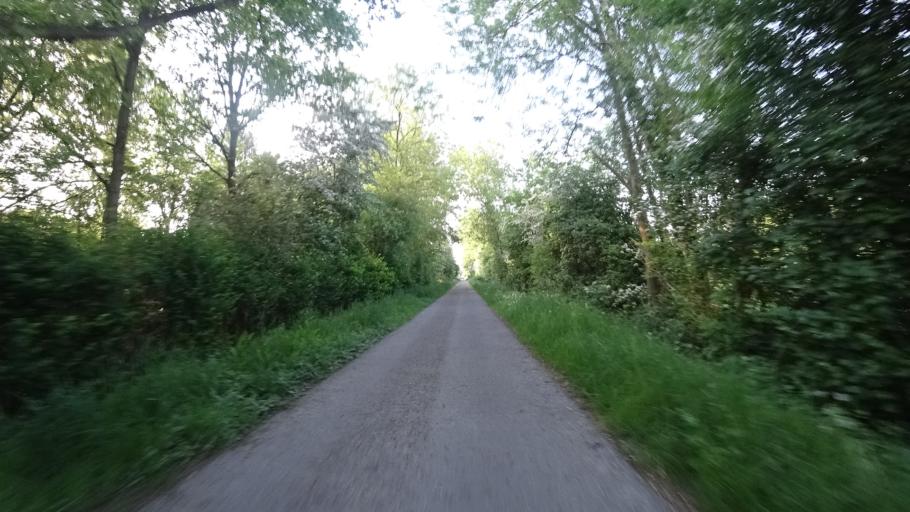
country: BE
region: Wallonia
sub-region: Province de Namur
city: Eghezee
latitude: 50.5892
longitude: 4.9092
